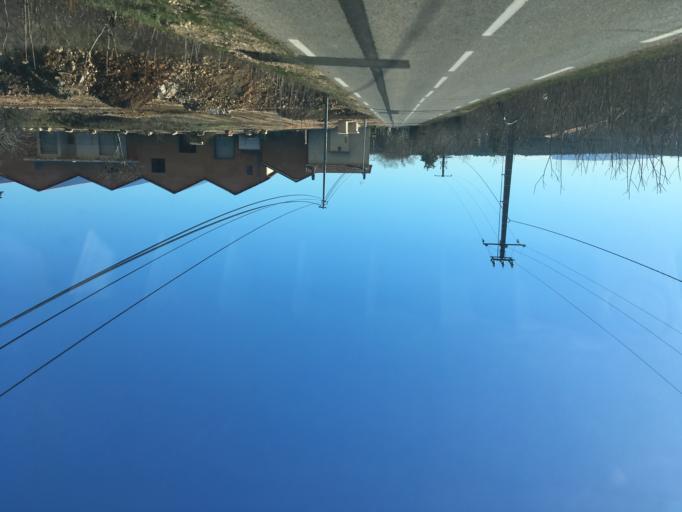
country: FR
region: Provence-Alpes-Cote d'Azur
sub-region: Departement du Var
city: Barjols
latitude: 43.5948
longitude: 6.0244
